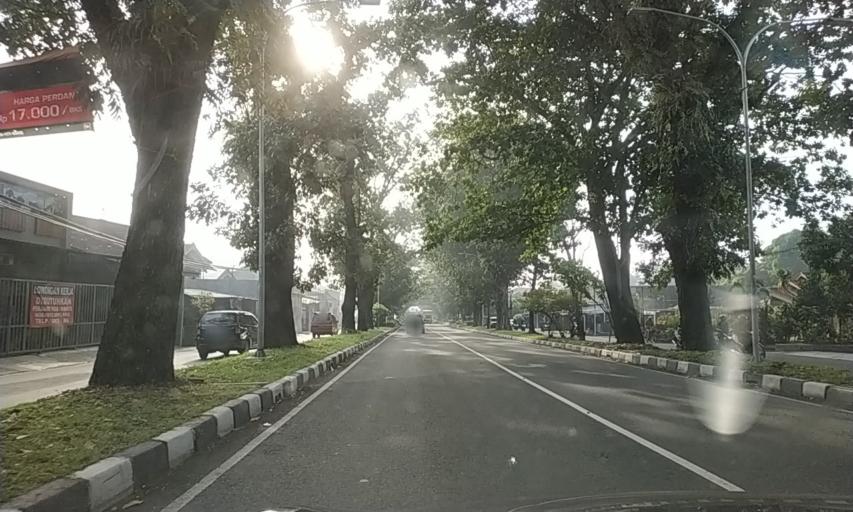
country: ID
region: Central Java
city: Candi Prambanan
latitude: -7.7567
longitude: 110.4826
